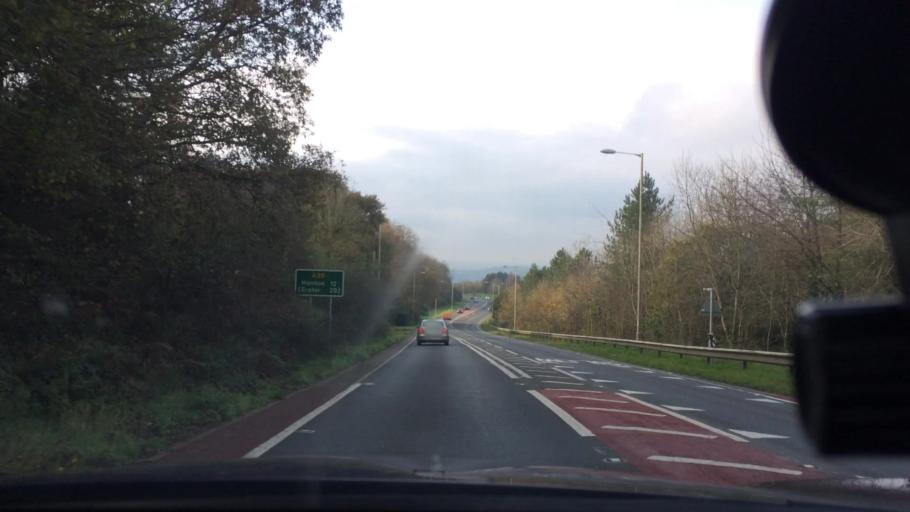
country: GB
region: England
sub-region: Devon
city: Axminster
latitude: 50.7643
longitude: -2.9736
